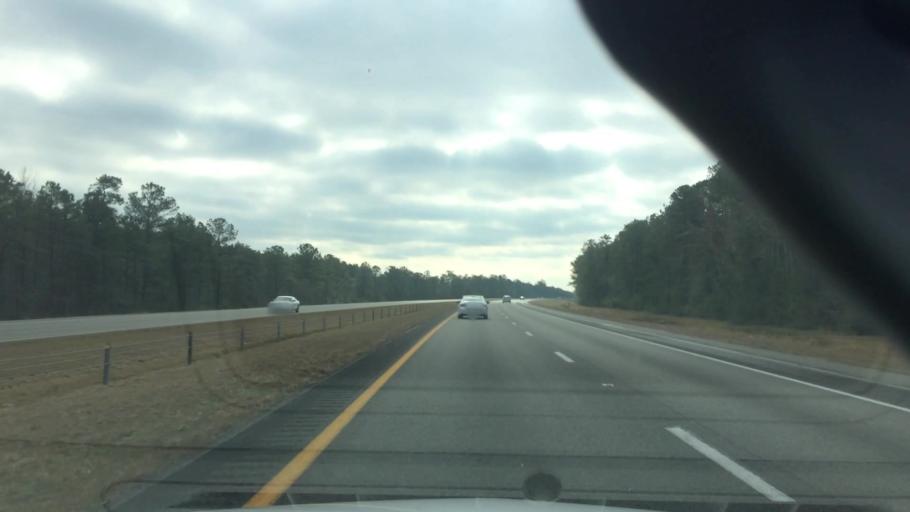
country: US
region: North Carolina
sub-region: New Hanover County
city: Castle Hayne
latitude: 34.3912
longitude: -77.8753
